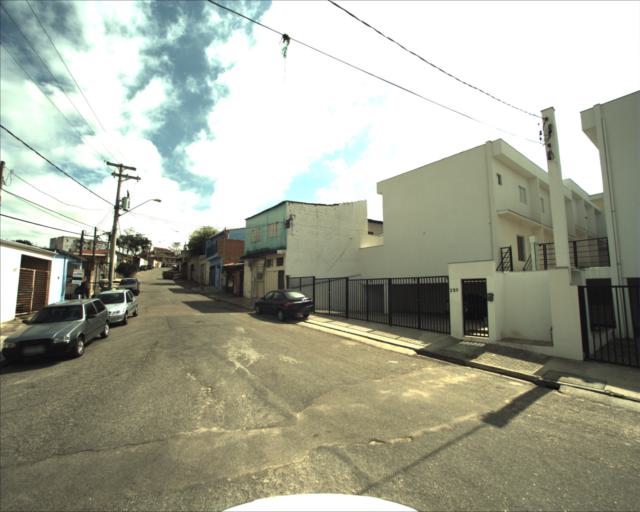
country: BR
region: Sao Paulo
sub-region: Sorocaba
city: Sorocaba
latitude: -23.4929
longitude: -47.4814
